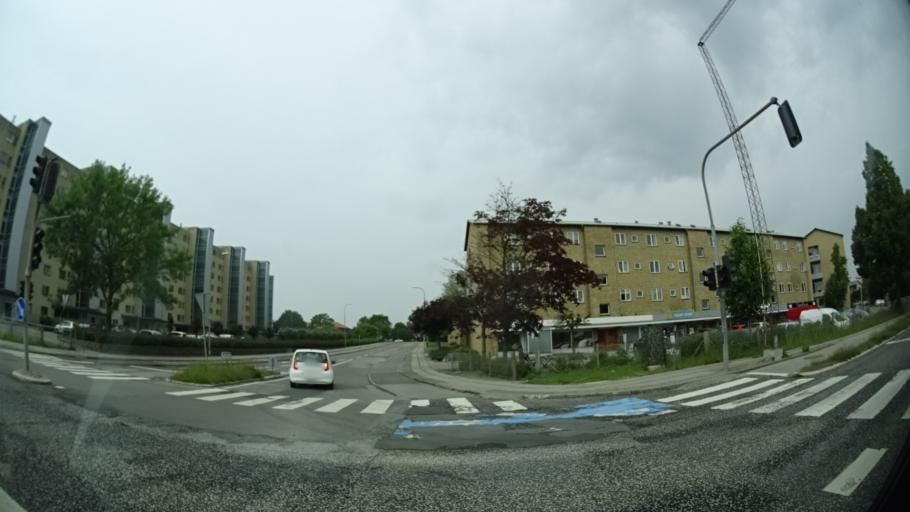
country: DK
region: Central Jutland
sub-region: Arhus Kommune
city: Arhus
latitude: 56.1924
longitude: 10.2185
